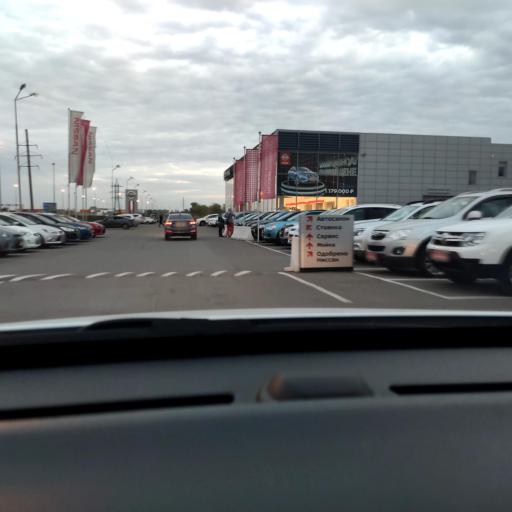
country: RU
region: Voronezj
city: Somovo
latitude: 51.6627
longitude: 39.3006
